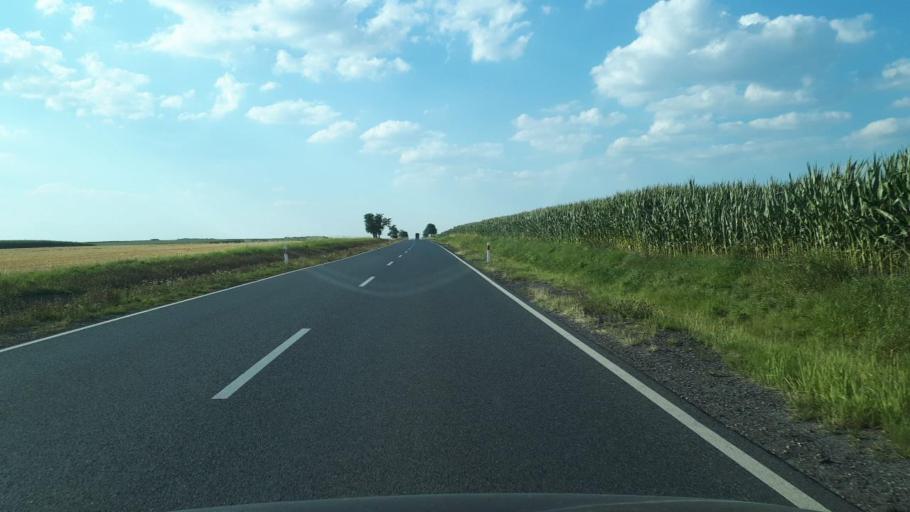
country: PL
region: Silesian Voivodeship
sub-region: Powiat gliwicki
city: Pyskowice
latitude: 50.4225
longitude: 18.6138
